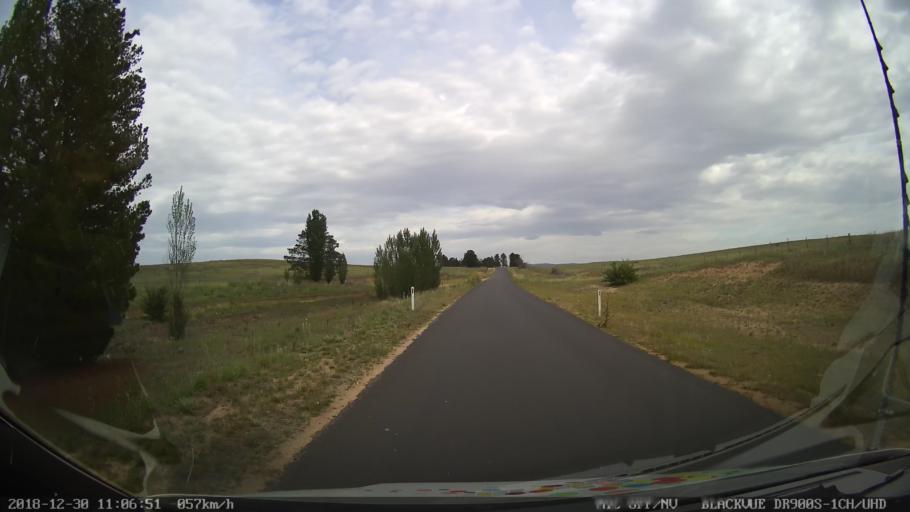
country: AU
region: New South Wales
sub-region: Snowy River
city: Berridale
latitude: -36.5039
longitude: 148.8266
